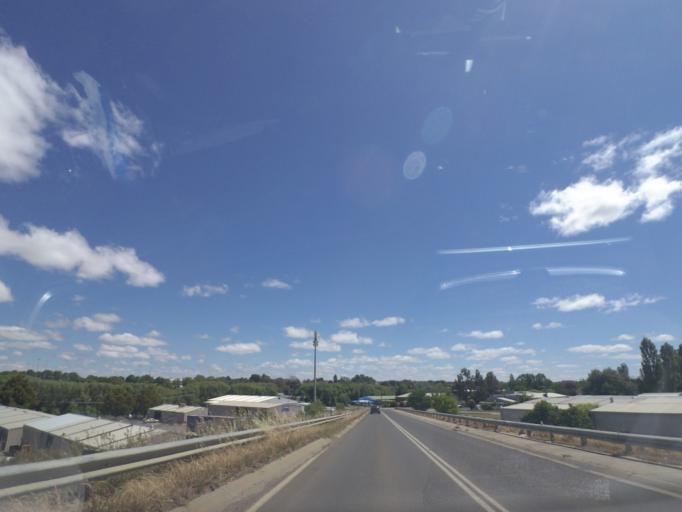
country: AU
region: Victoria
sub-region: Mount Alexander
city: Castlemaine
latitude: -37.2394
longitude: 144.4564
